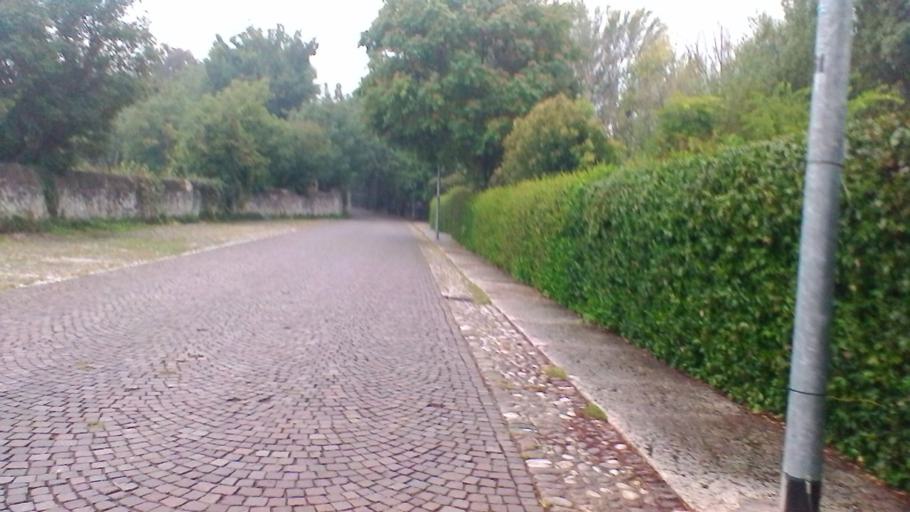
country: IT
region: Veneto
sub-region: Provincia di Verona
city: San Giovanni Lupatoto
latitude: 45.4225
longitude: 11.0441
